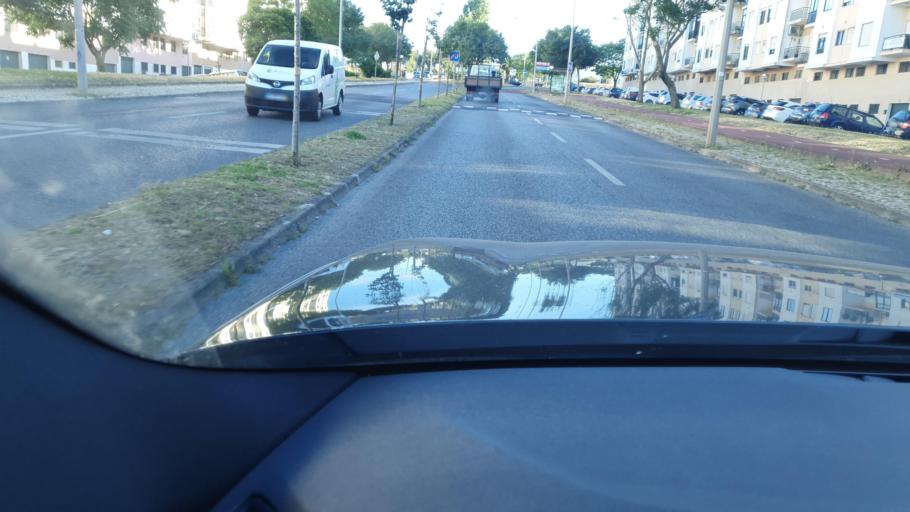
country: PT
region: Lisbon
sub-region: Sintra
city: Cacem
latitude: 38.7641
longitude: -9.2788
